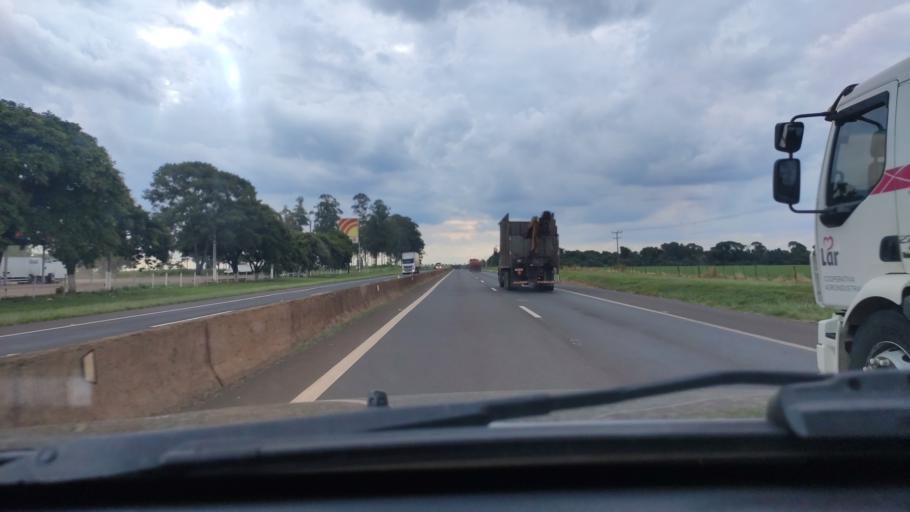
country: BR
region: Sao Paulo
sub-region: Palmital
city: Palmital
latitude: -22.8360
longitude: -50.0211
